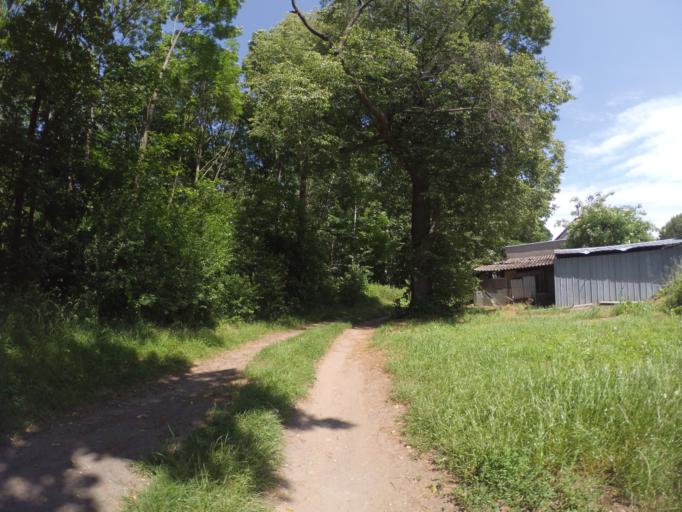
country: CZ
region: Central Bohemia
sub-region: Okres Nymburk
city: Sadska
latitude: 50.1706
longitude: 14.9402
